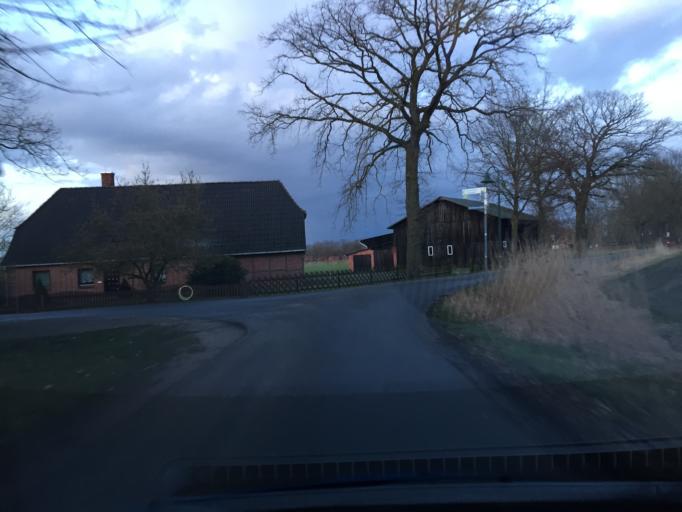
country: DE
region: Lower Saxony
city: Ludersburg
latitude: 53.3068
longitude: 10.6119
